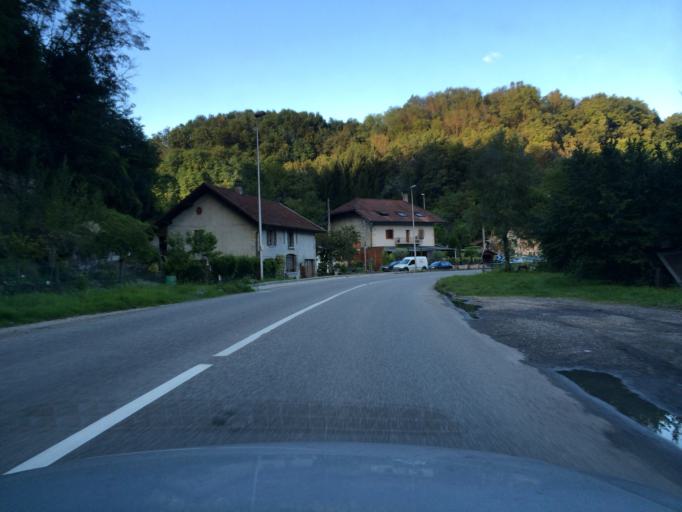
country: FR
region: Rhone-Alpes
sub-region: Departement de la Haute-Savoie
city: Frangy
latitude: 46.0273
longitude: 5.8886
